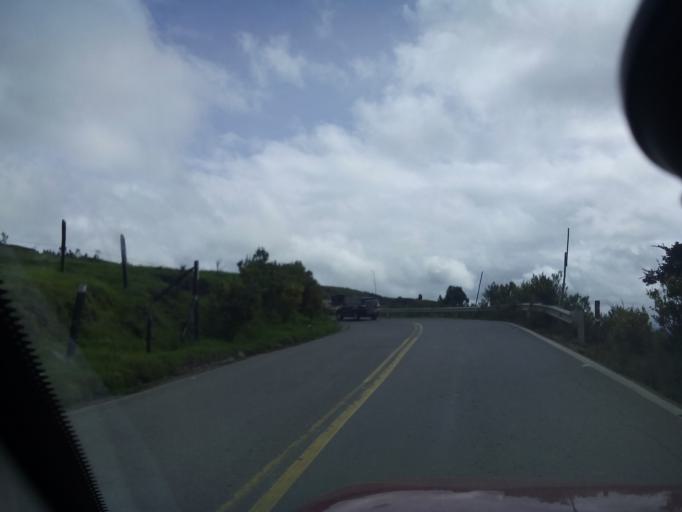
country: CO
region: Boyaca
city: Combita
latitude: 5.6360
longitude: -73.3400
